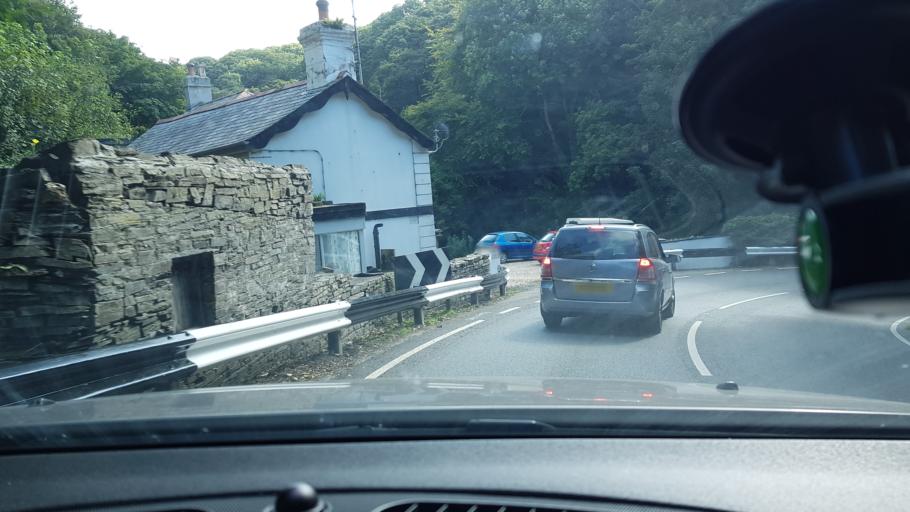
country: GB
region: England
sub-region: Cornwall
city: Tintagel
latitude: 50.6690
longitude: -4.7274
